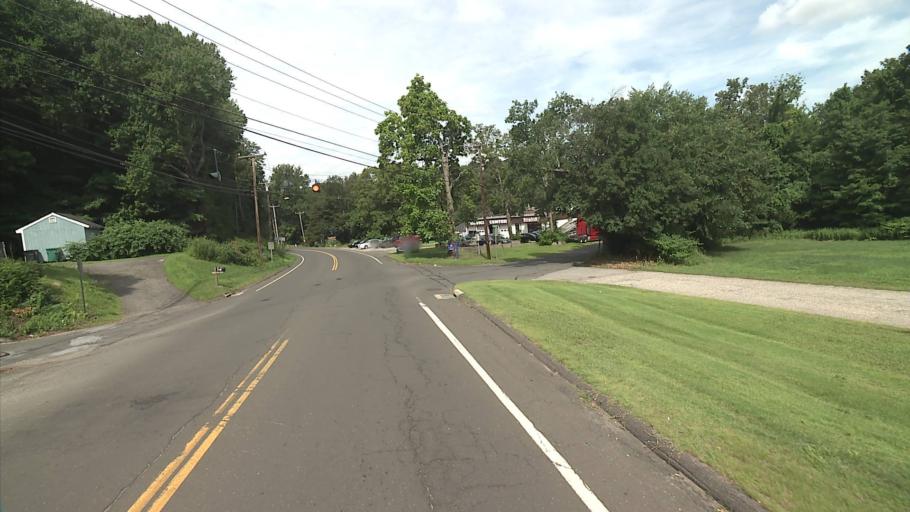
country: US
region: Connecticut
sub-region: New Haven County
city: Seymour
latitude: 41.3982
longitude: -73.0508
